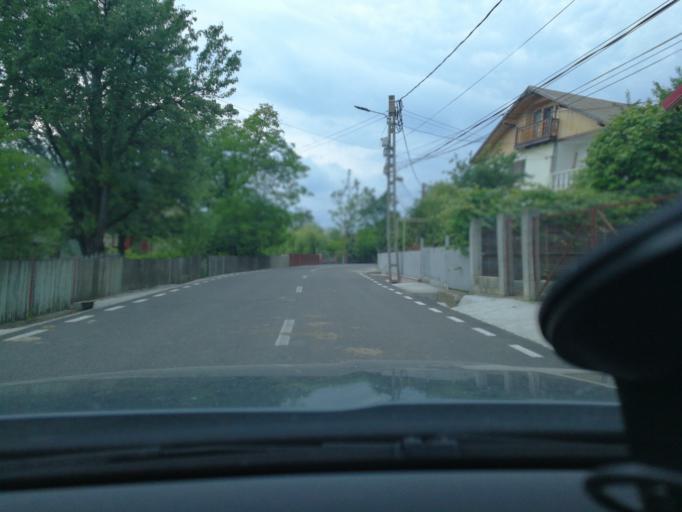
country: RO
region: Prahova
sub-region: Comuna Cornu
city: Cornu de Jos
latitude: 45.1535
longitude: 25.7177
